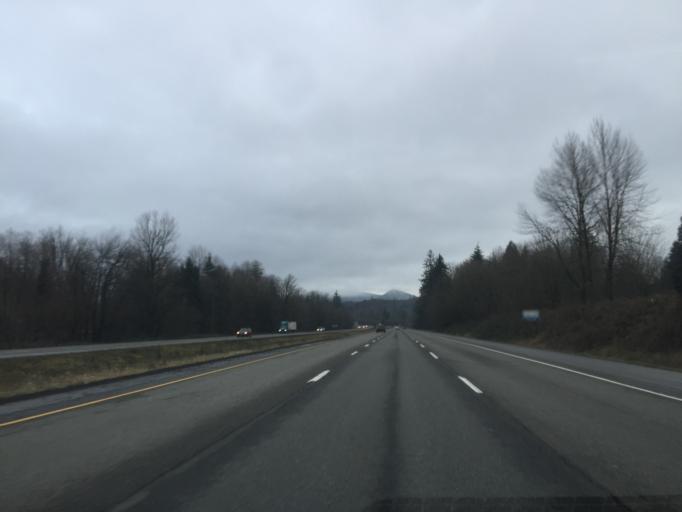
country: US
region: Washington
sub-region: King County
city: North Bend
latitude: 47.4814
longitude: -121.7897
